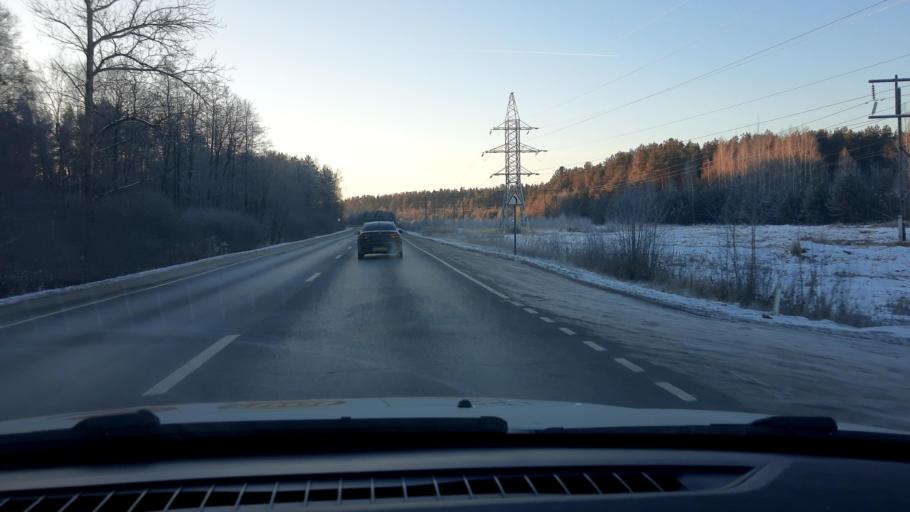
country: RU
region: Nizjnij Novgorod
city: Lukino
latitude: 56.4309
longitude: 43.6271
